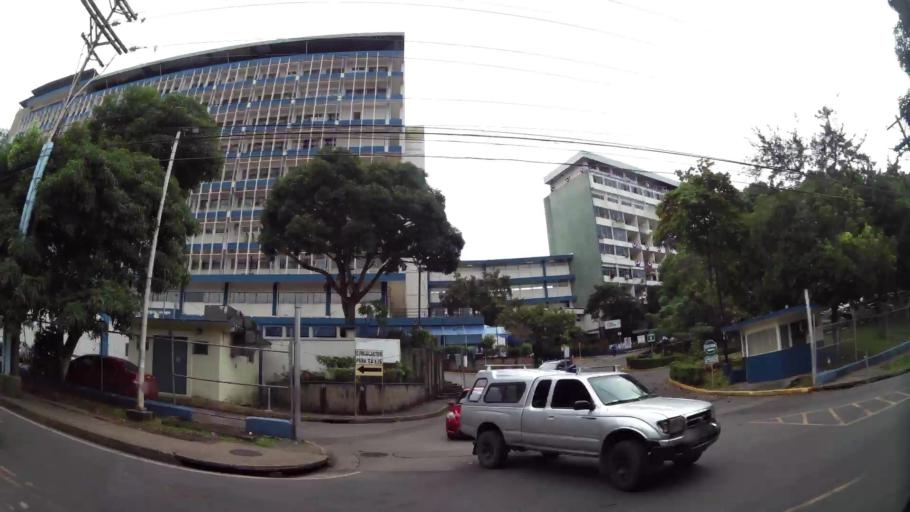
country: PA
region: Panama
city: Panama
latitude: 8.9814
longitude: -79.5347
